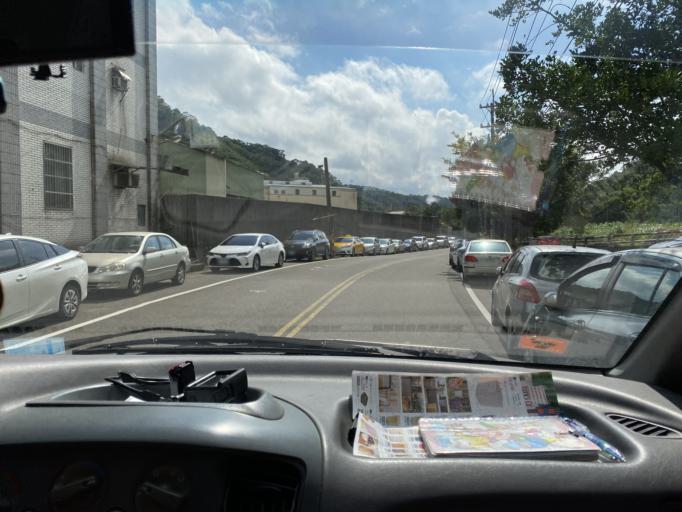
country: TW
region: Taiwan
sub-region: Hsinchu
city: Zhubei
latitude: 24.7436
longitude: 121.1358
